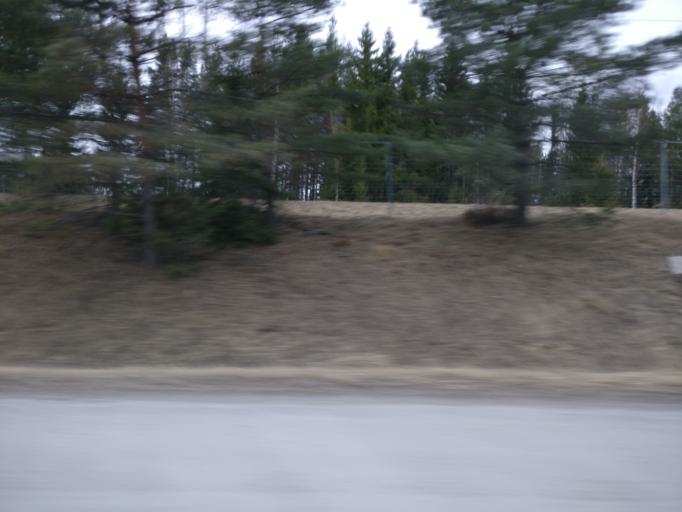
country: FI
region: Uusimaa
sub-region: Helsinki
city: Nurmijaervi
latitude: 60.4926
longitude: 24.8511
